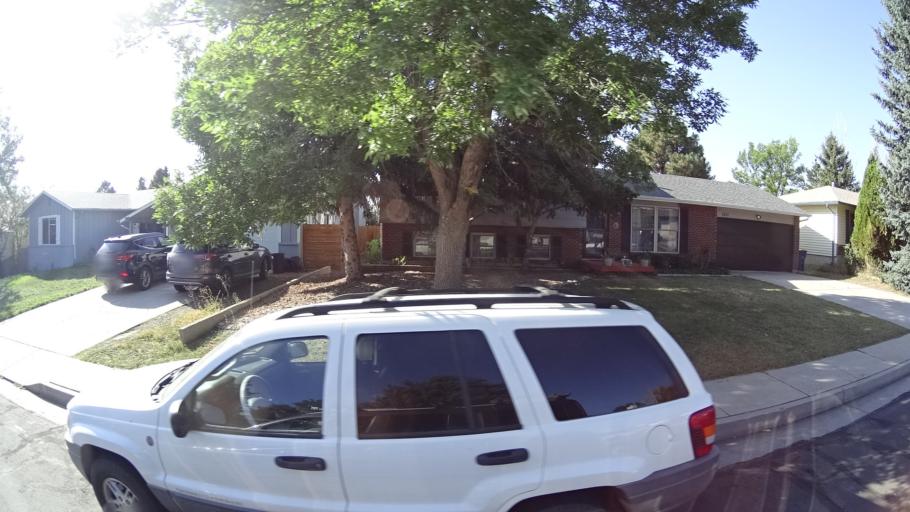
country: US
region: Colorado
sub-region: El Paso County
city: Cimarron Hills
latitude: 38.8841
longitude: -104.7232
